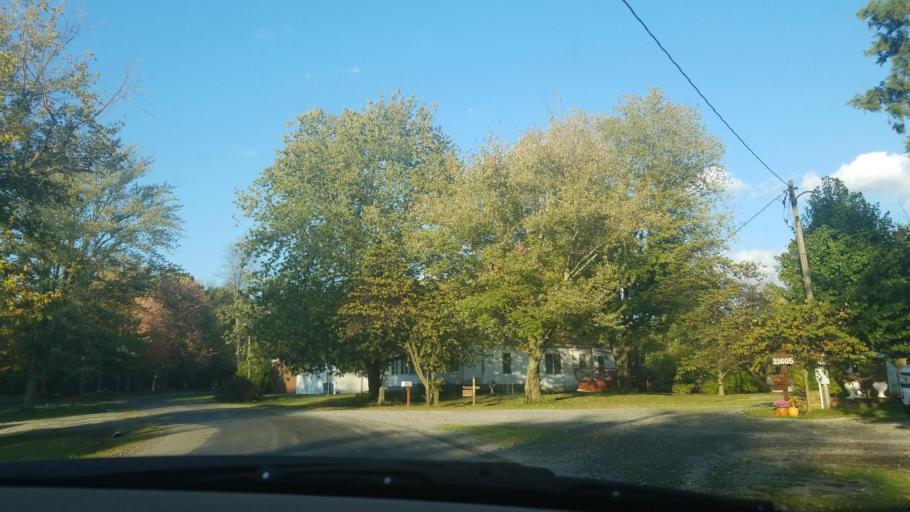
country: US
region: Illinois
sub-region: Saline County
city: Carrier Mills
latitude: 37.7681
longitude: -88.7725
